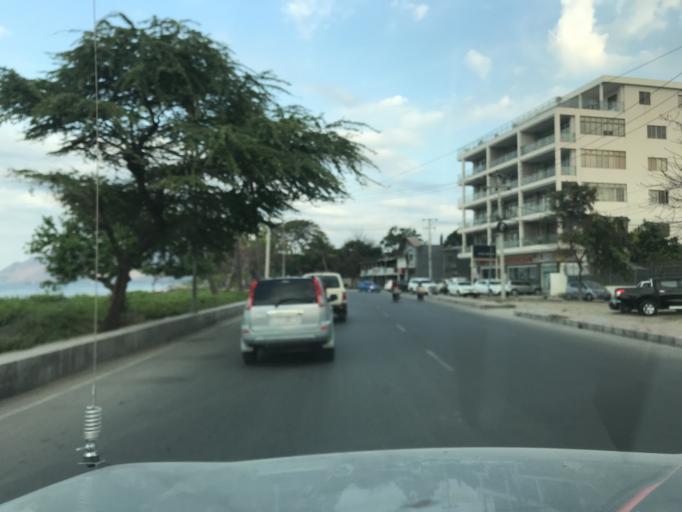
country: TL
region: Dili
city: Dili
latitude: -8.5480
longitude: 125.5586
